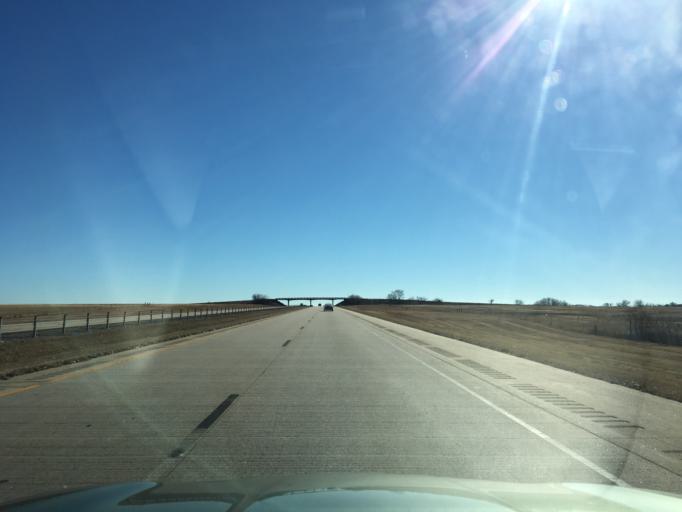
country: US
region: Oklahoma
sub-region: Kay County
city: Tonkawa
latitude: 36.4965
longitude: -97.3325
